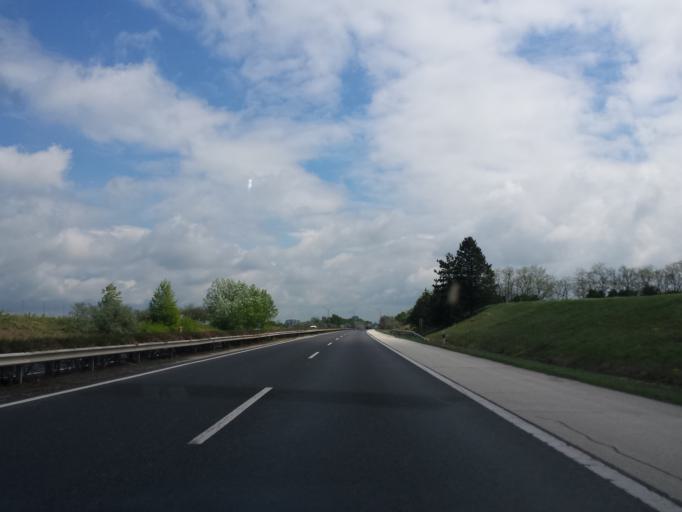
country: HU
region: Komarom-Esztergom
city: Acs
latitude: 47.6825
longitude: 18.0191
